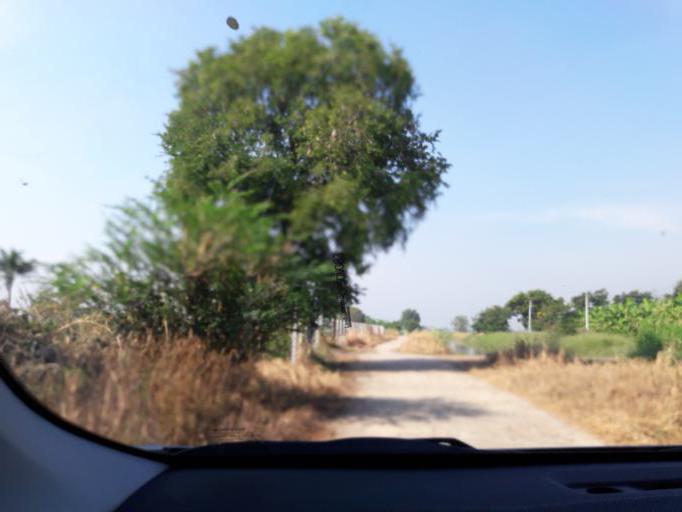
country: TH
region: Ang Thong
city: Ang Thong
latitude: 14.5897
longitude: 100.4228
